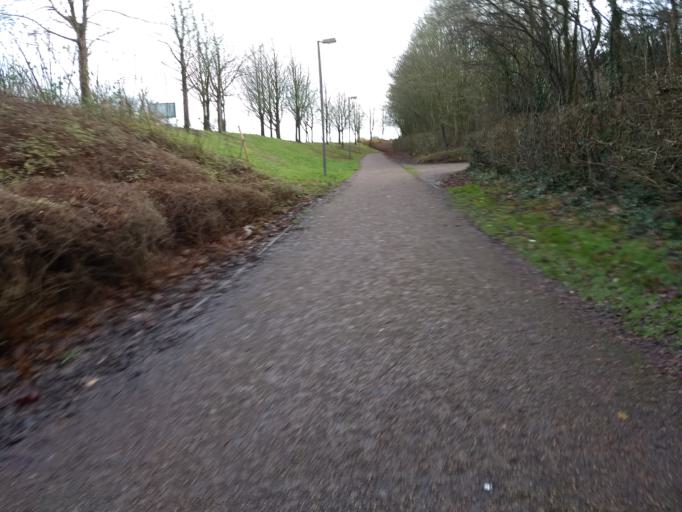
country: GB
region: England
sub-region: Buckinghamshire
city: Newton Longville
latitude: 51.9988
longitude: -0.7744
